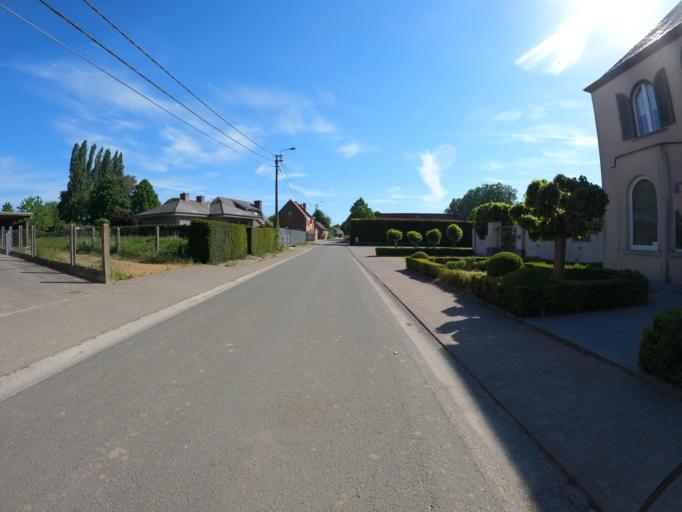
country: BE
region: Flanders
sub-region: Provincie Oost-Vlaanderen
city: Oosterzele
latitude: 50.9239
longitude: 3.7848
